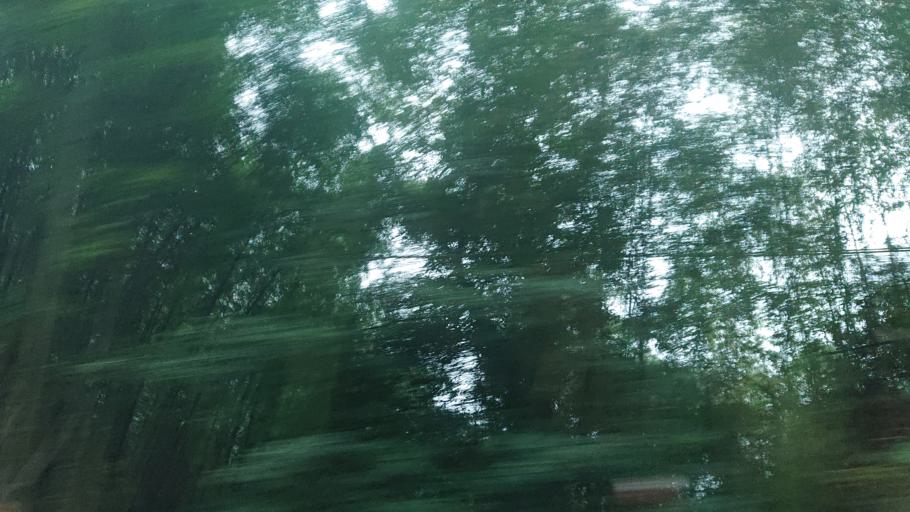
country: TW
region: Taiwan
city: Lugu
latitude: 23.5077
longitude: 120.7027
